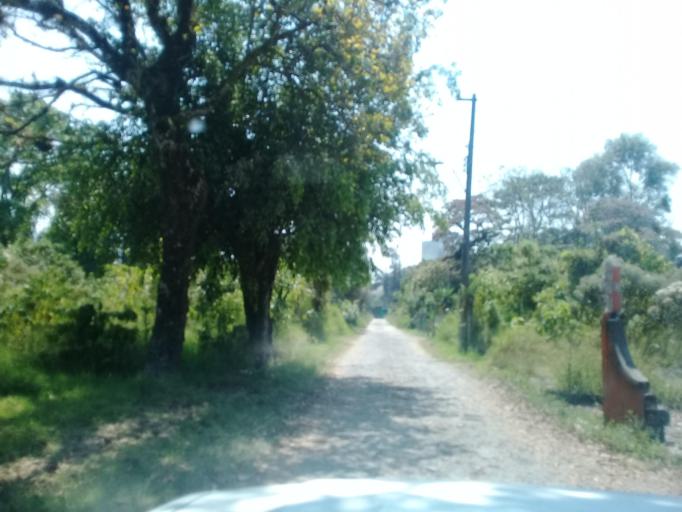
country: MX
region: Veracruz
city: Ixtac Zoquitlan
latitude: 18.8629
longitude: -97.0412
